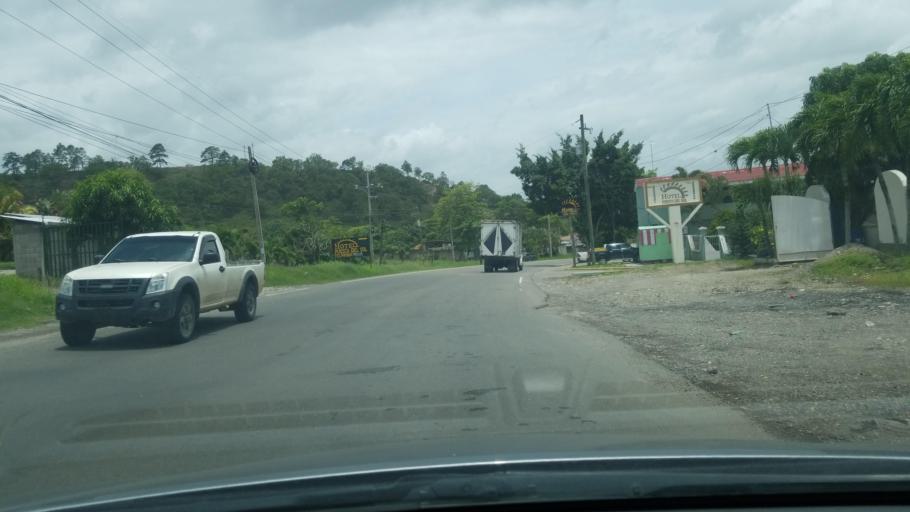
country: HN
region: Copan
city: Cucuyagua
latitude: 14.6671
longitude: -88.8665
